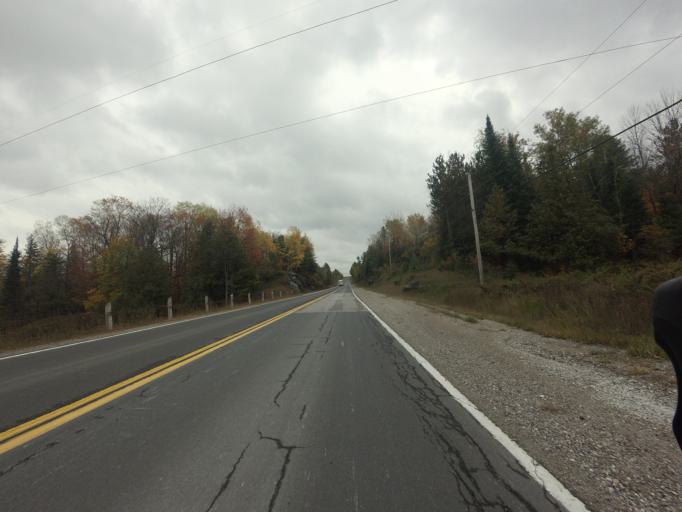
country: CA
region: Ontario
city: Perth
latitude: 45.1122
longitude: -76.4828
